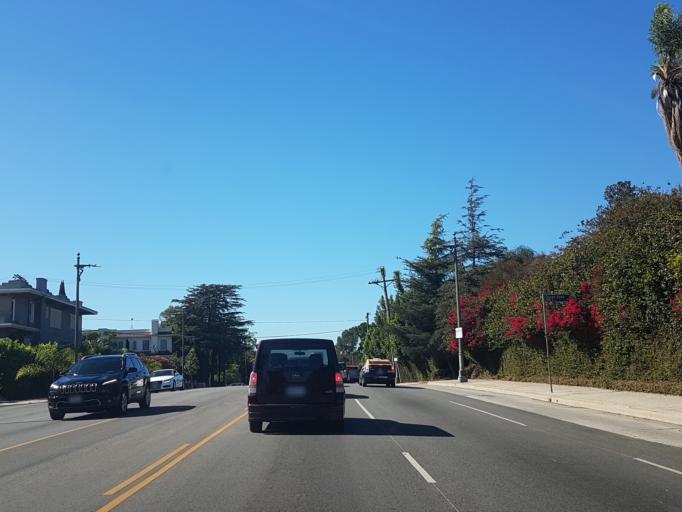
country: US
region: California
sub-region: Los Angeles County
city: Hollywood
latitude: 34.0557
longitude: -118.3295
